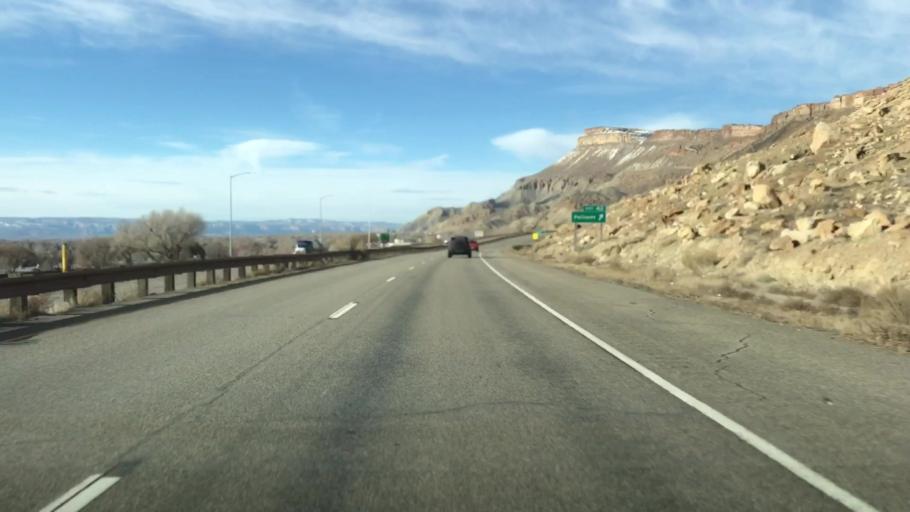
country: US
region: Colorado
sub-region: Mesa County
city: Palisade
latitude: 39.1169
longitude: -108.3523
